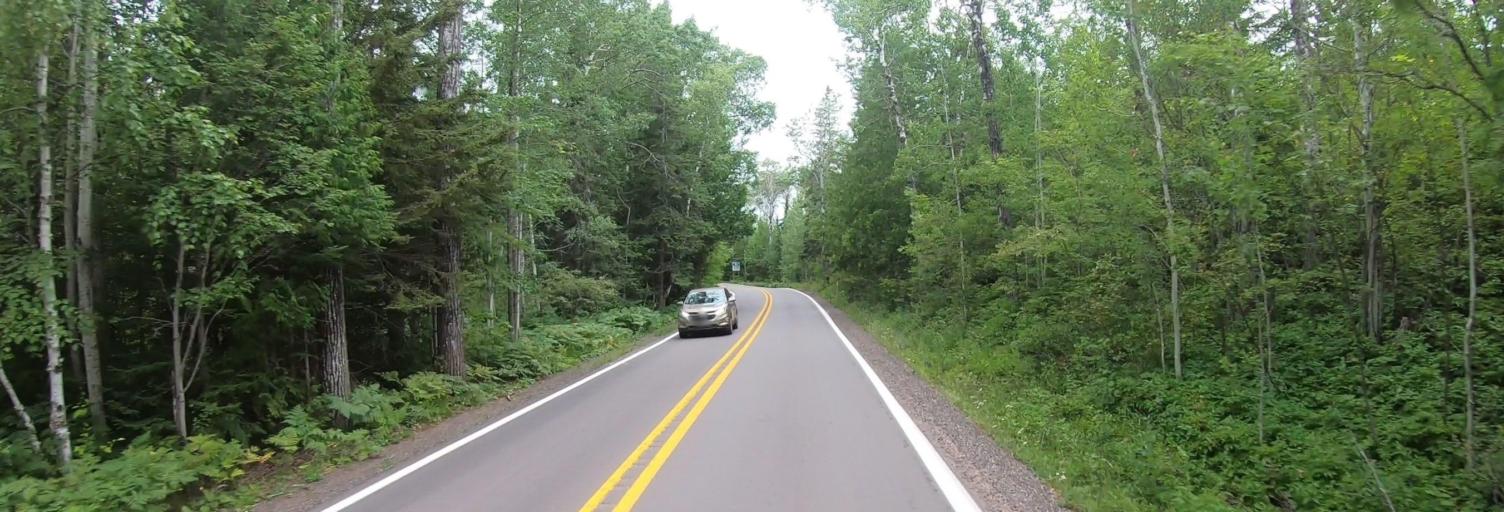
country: US
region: Michigan
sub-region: Keweenaw County
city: Eagle River
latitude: 47.4628
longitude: -88.0739
